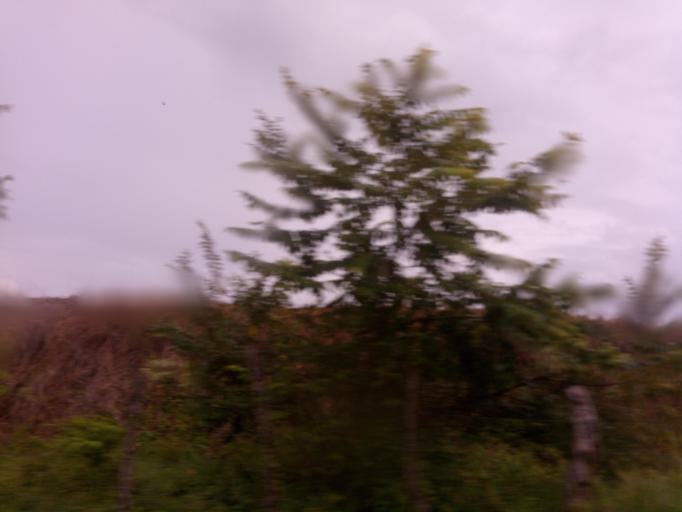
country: PA
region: Los Santos
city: Pedasi
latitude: 7.6185
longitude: -80.0853
